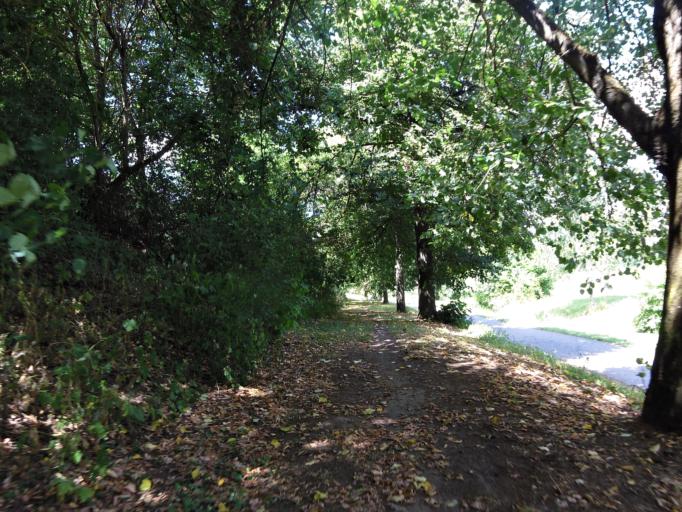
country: DE
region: Bavaria
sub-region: Regierungsbezirk Unterfranken
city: Gerbrunn
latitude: 49.7852
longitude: 9.9974
